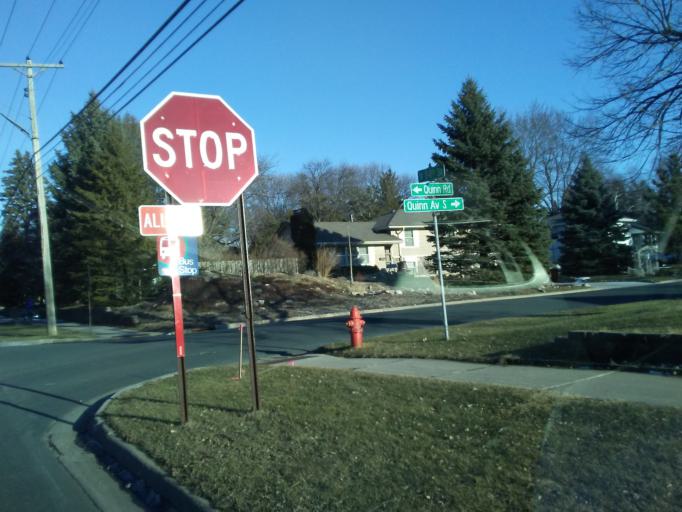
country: US
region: Minnesota
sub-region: Hennepin County
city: Edina
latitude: 44.8516
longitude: -93.3439
